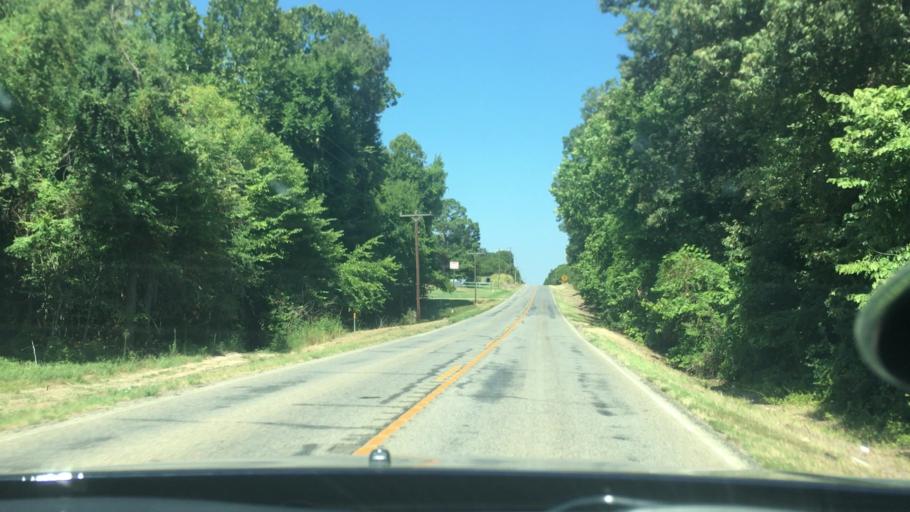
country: US
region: Oklahoma
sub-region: Johnston County
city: Tishomingo
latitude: 34.2378
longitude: -96.5923
